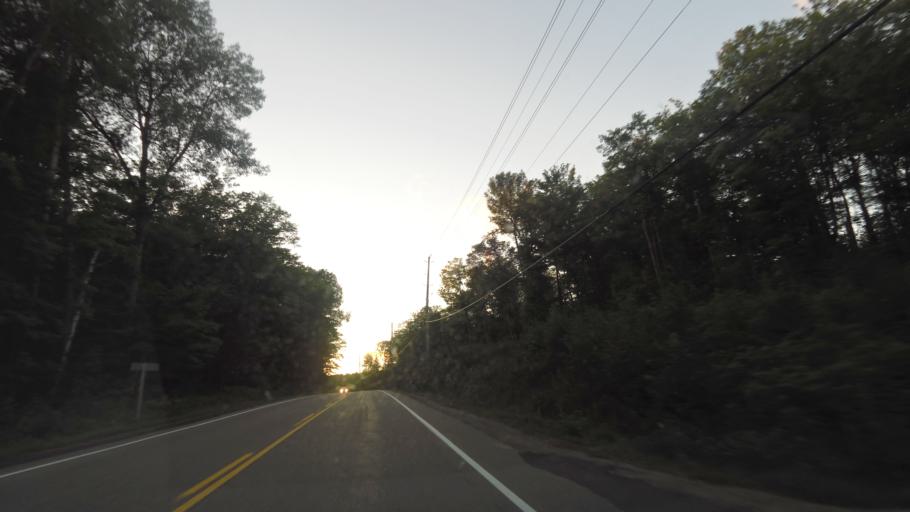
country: CA
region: Ontario
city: Bancroft
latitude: 45.0281
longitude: -78.3912
